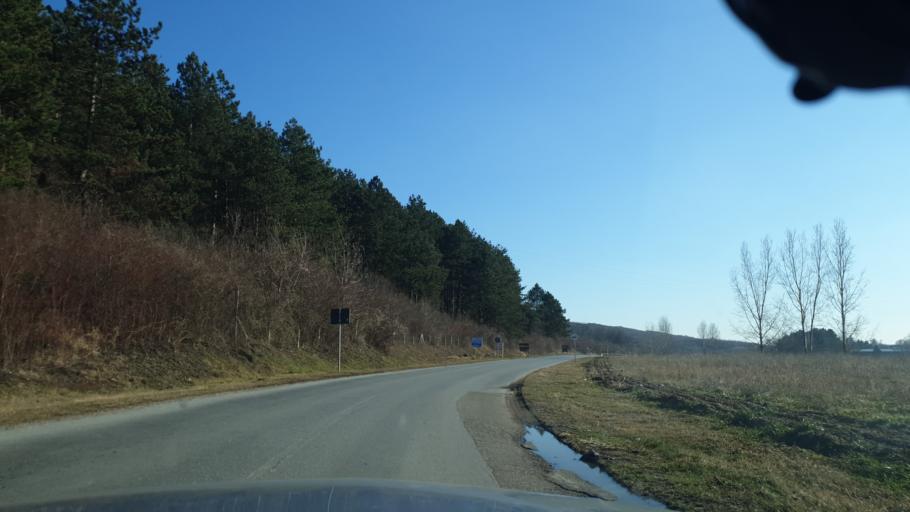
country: RS
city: Vrdnik
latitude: 45.1141
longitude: 19.7988
